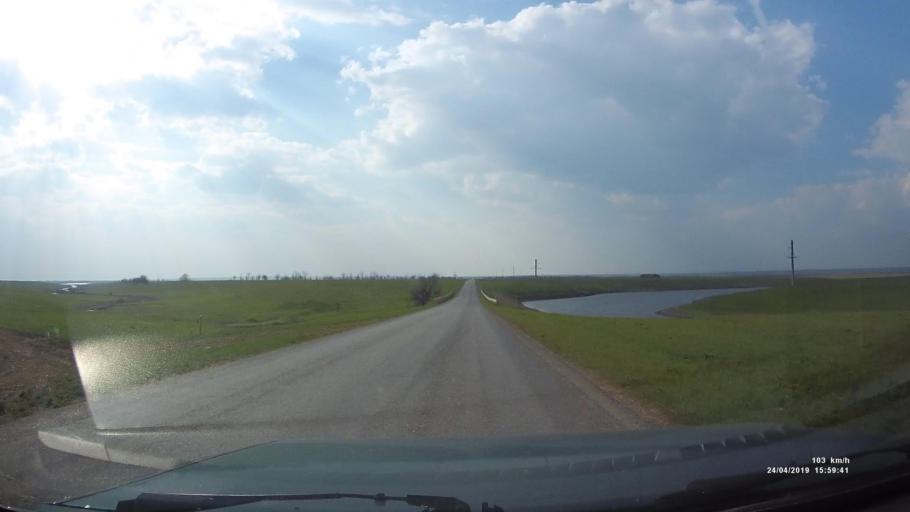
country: RU
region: Rostov
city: Sovetskoye
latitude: 46.6257
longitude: 42.4675
